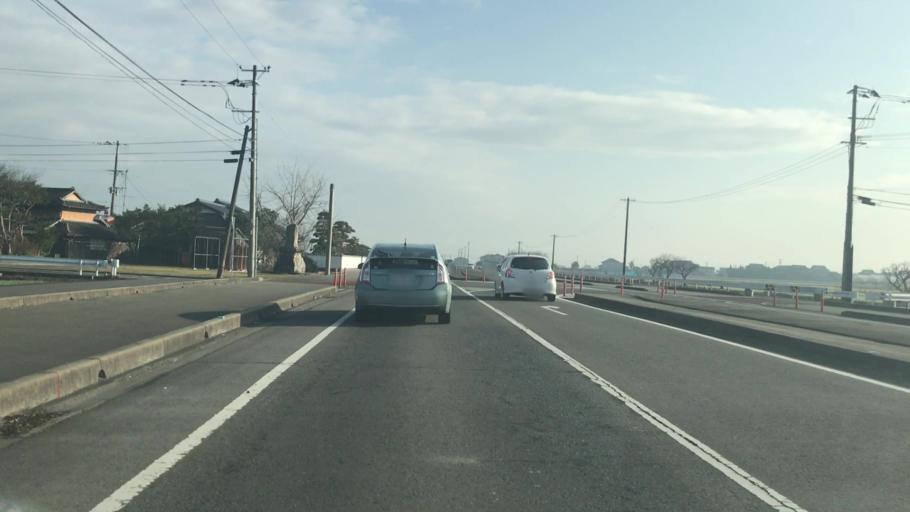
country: JP
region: Saga Prefecture
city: Saga-shi
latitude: 33.2181
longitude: 130.1732
